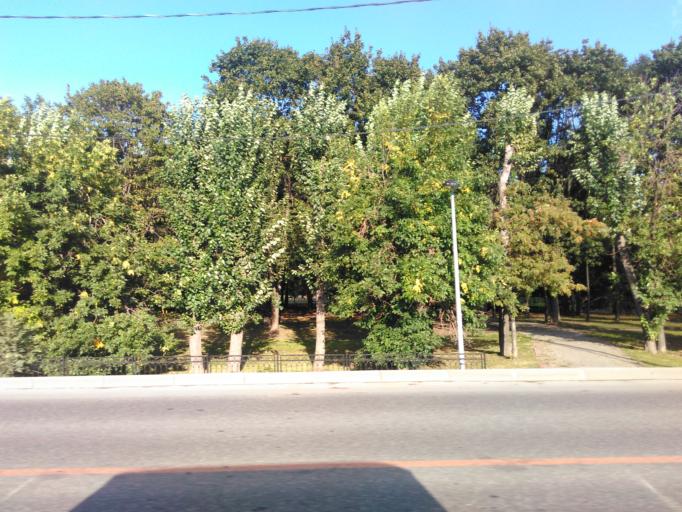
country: RU
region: Moscow
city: Zapadnoye Degunino
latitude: 55.8671
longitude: 37.5474
